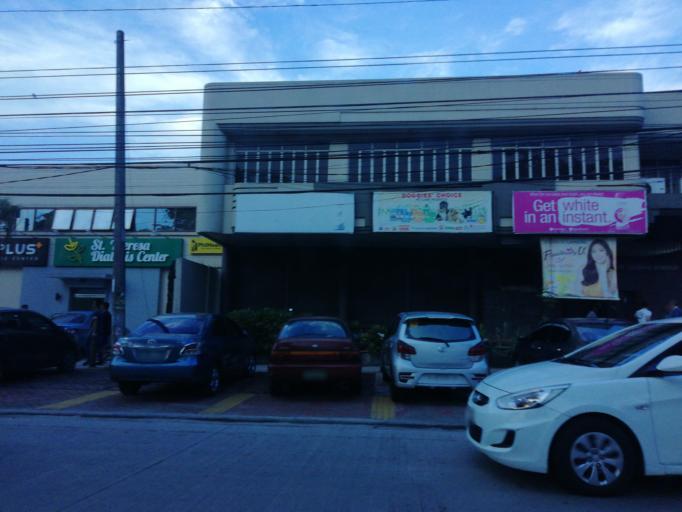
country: PH
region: Metro Manila
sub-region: Quezon City
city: Quezon City
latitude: 14.6581
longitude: 121.0452
